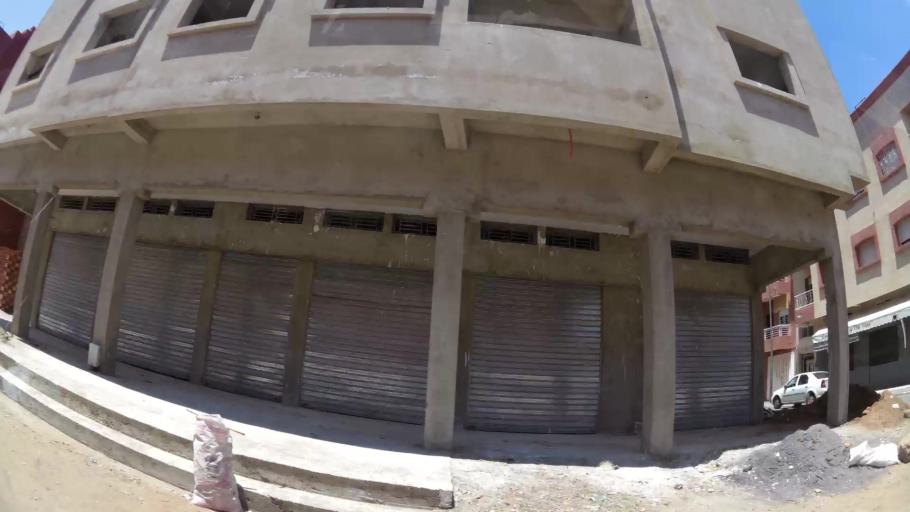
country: MA
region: Gharb-Chrarda-Beni Hssen
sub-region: Kenitra Province
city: Kenitra
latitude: 34.2521
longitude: -6.6251
